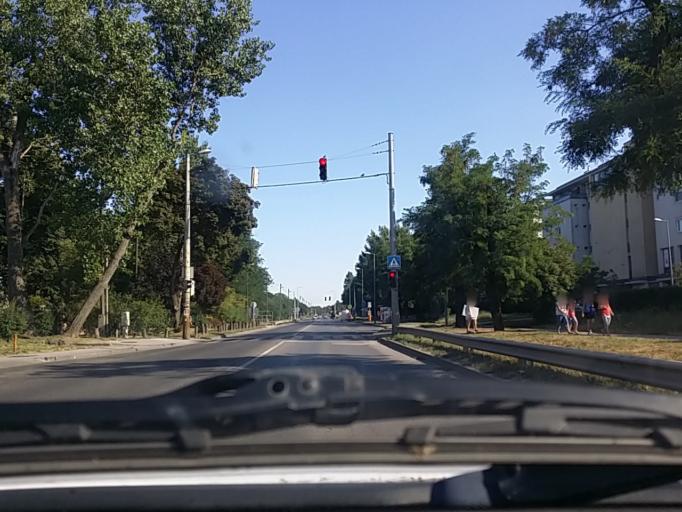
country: HU
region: Pest
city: Urom
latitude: 47.5728
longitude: 19.0163
